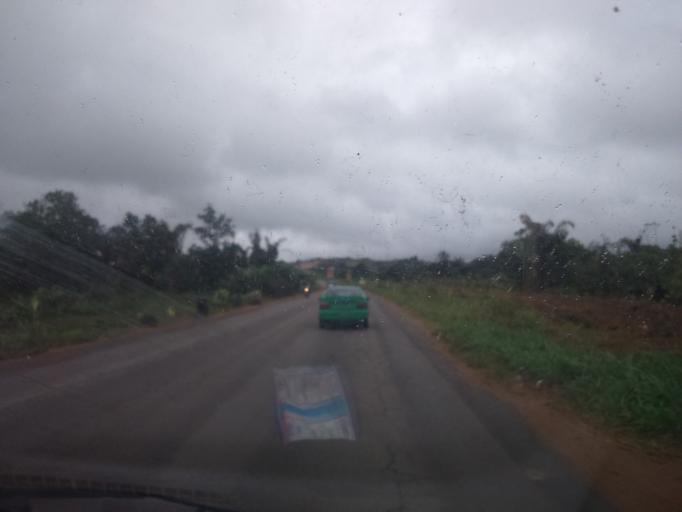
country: CI
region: Sud-Comoe
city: Bonoua
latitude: 5.2487
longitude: -3.6204
